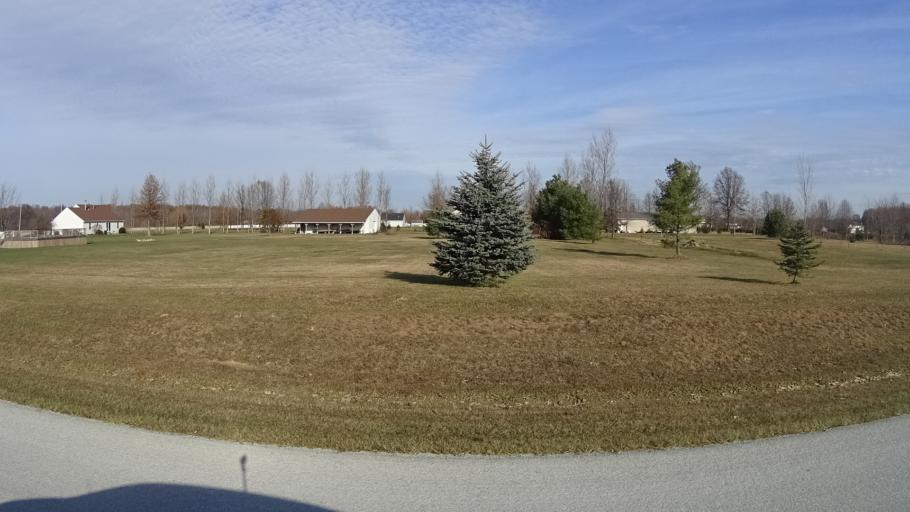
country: US
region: Ohio
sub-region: Lorain County
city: Grafton
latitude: 41.2184
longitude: -82.0416
